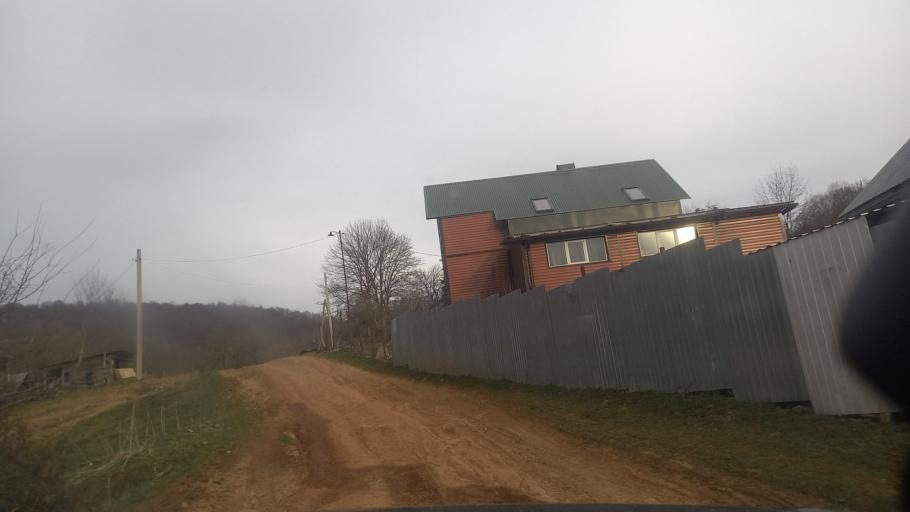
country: RU
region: Adygeya
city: Kamennomostskiy
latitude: 44.2111
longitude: 40.0212
